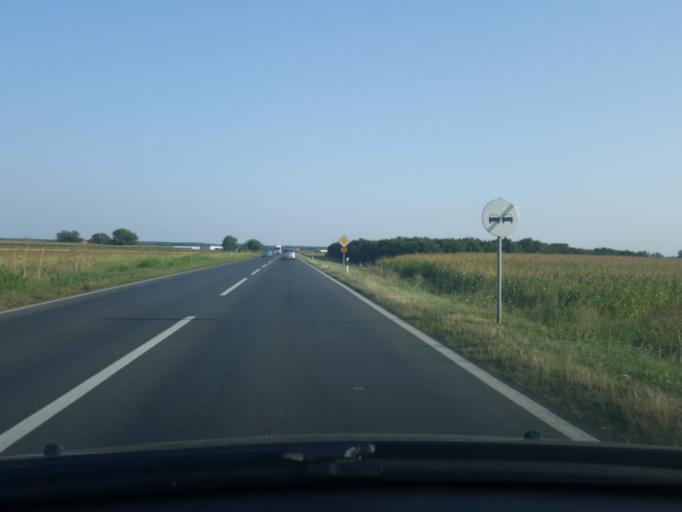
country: RS
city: Klenak
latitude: 44.7830
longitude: 19.7234
